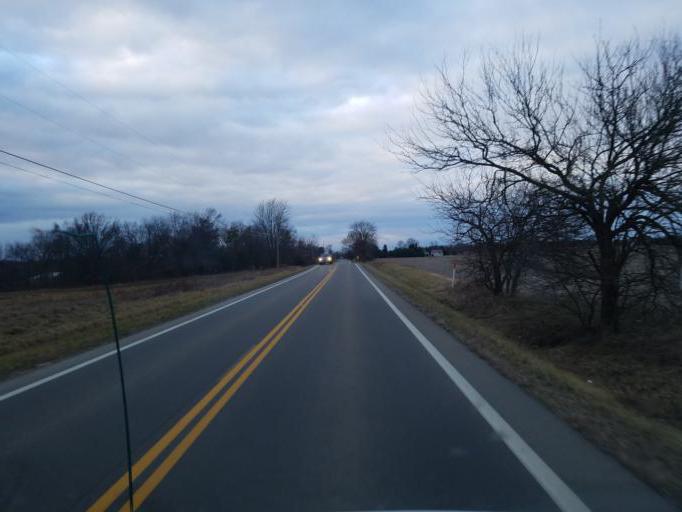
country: US
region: Ohio
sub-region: Delaware County
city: Delaware
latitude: 40.3333
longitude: -83.1315
